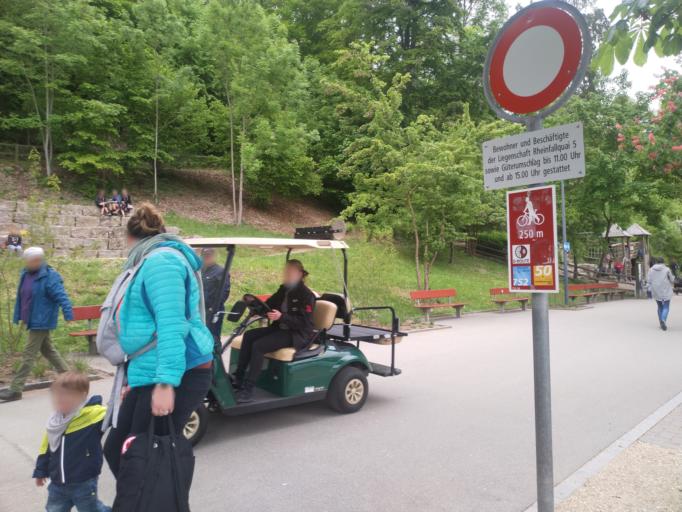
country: CH
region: Schaffhausen
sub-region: Bezirk Schaffhausen
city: Neuhausen
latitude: 47.6787
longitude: 8.6116
